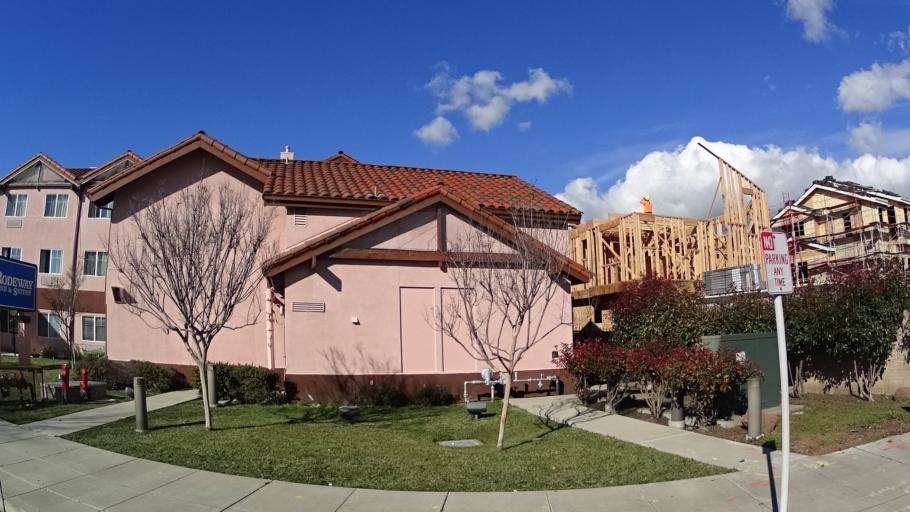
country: US
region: California
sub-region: Alameda County
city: San Lorenzo
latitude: 37.6659
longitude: -122.1156
